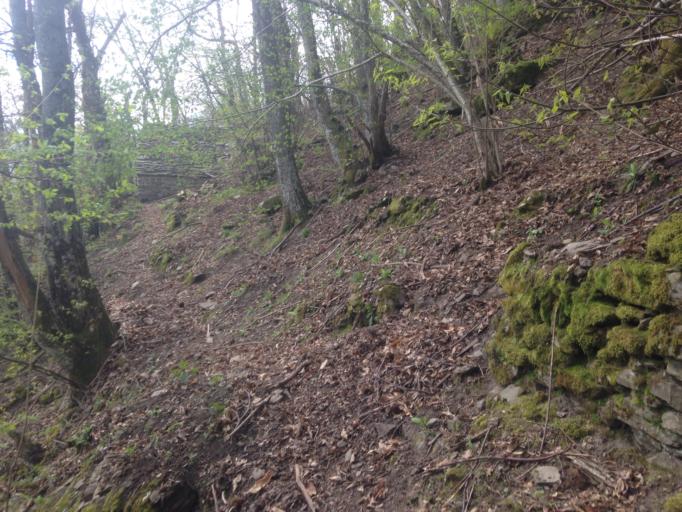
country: IT
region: Emilia-Romagna
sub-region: Provincia di Bologna
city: Lizzano in Belvedere
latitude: 44.1555
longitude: 10.8888
